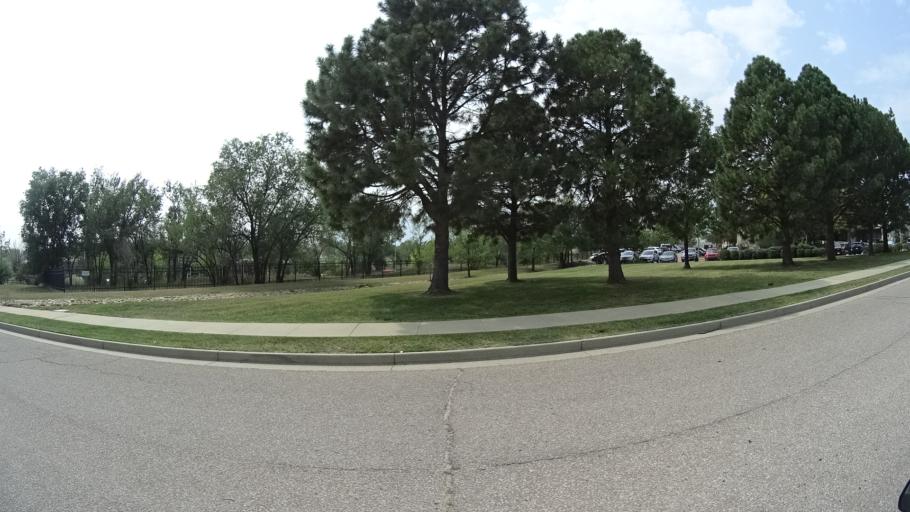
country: US
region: Colorado
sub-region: El Paso County
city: Colorado Springs
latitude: 38.8276
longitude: -104.7899
